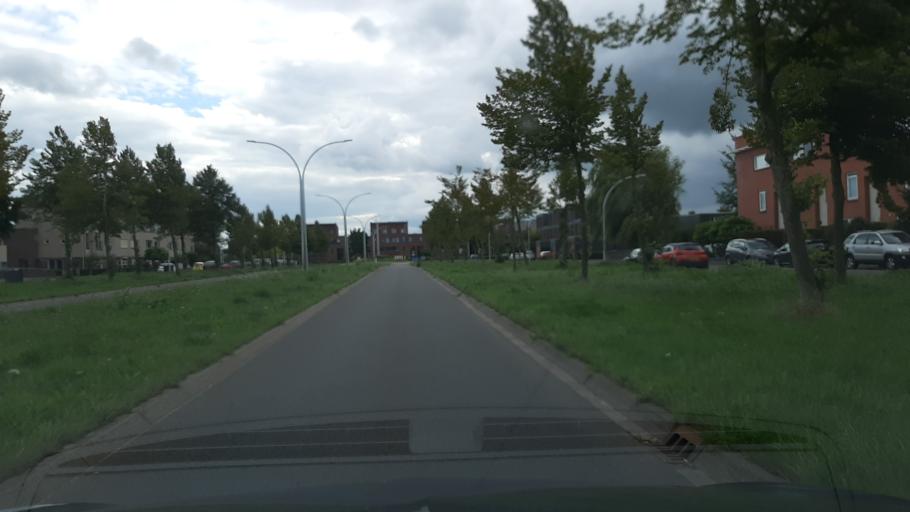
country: NL
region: Overijssel
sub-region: Gemeente Zwolle
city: Zwolle
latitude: 52.5401
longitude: 6.0537
